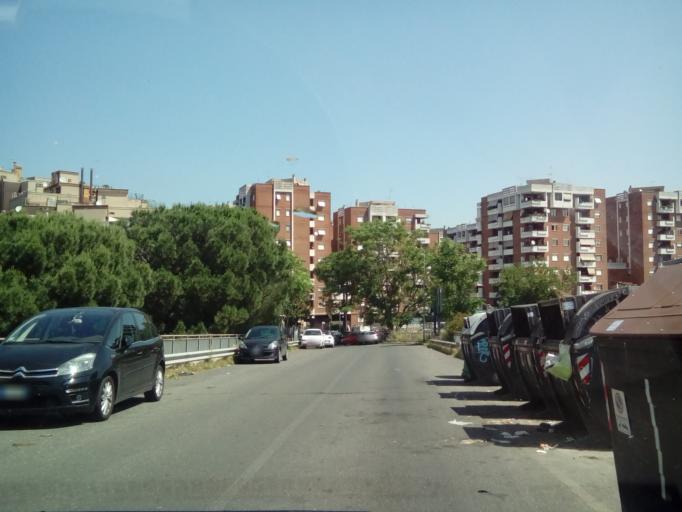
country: IT
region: Latium
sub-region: Citta metropolitana di Roma Capitale
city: Rome
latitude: 41.8816
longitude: 12.5910
